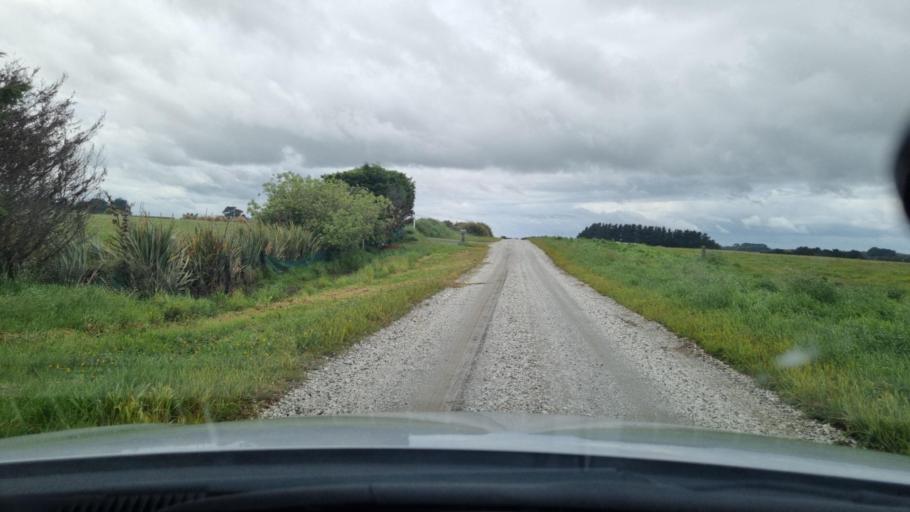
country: NZ
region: Southland
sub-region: Invercargill City
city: Invercargill
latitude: -46.4552
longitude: 168.3851
